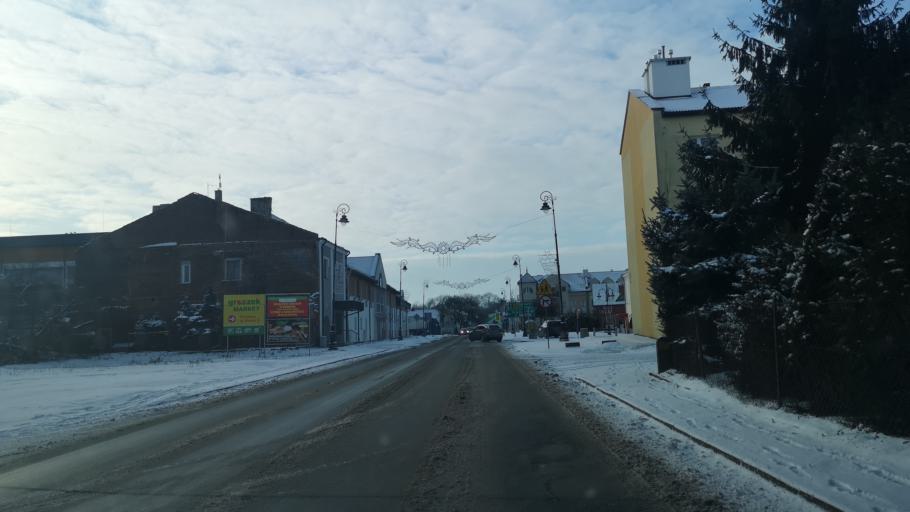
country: PL
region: Subcarpathian Voivodeship
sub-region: Powiat przeworski
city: Sieniawa
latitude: 50.1791
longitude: 22.6099
